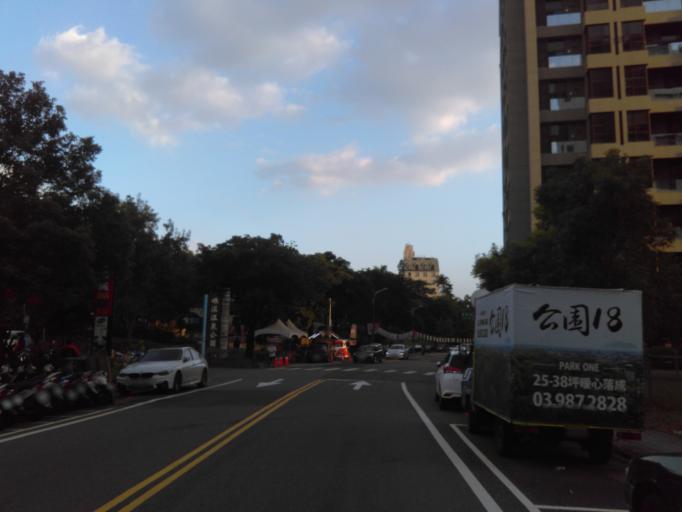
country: TW
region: Taiwan
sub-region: Yilan
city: Yilan
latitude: 24.8316
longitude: 121.7754
